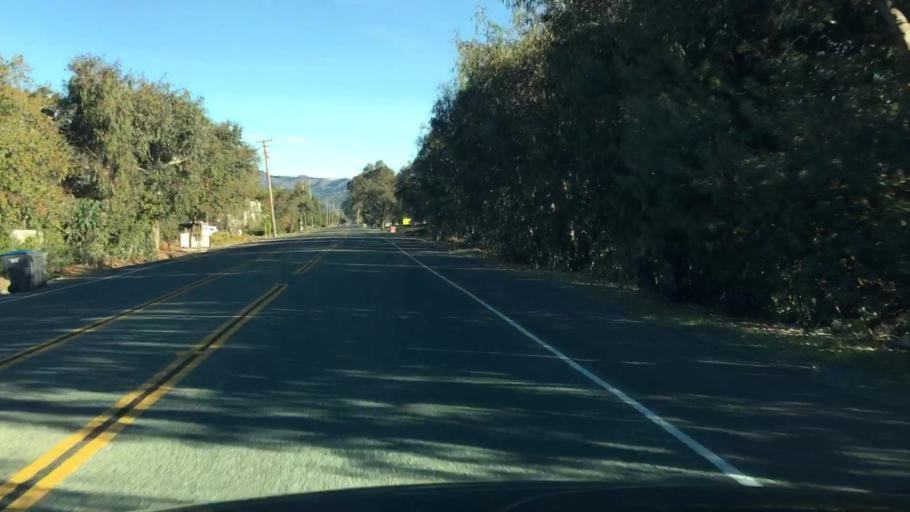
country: US
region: California
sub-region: Sonoma County
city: Sonoma
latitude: 38.2581
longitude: -122.4407
